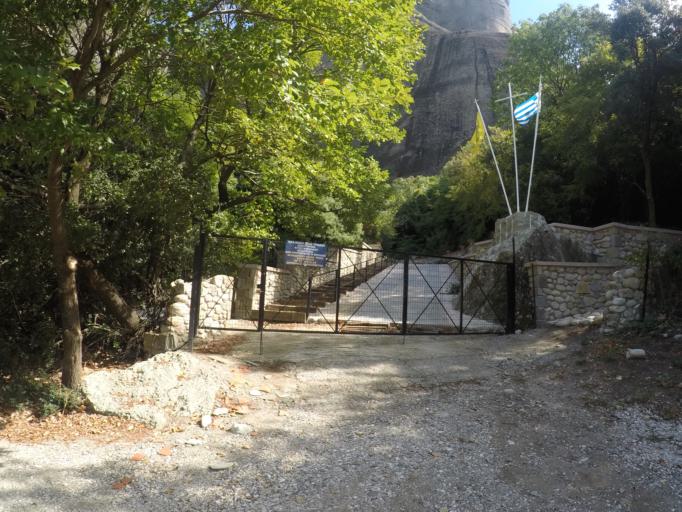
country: GR
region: Thessaly
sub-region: Trikala
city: Kastraki
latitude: 39.7115
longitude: 21.6212
